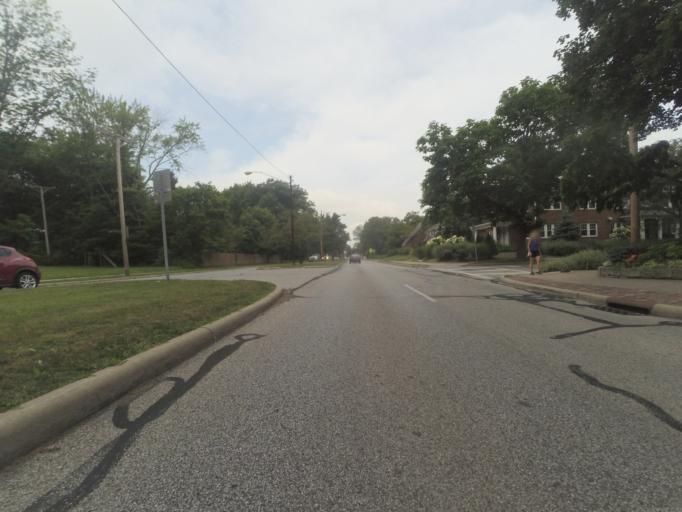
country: US
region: Ohio
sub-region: Cuyahoga County
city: University Heights
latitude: 41.4865
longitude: -81.5568
